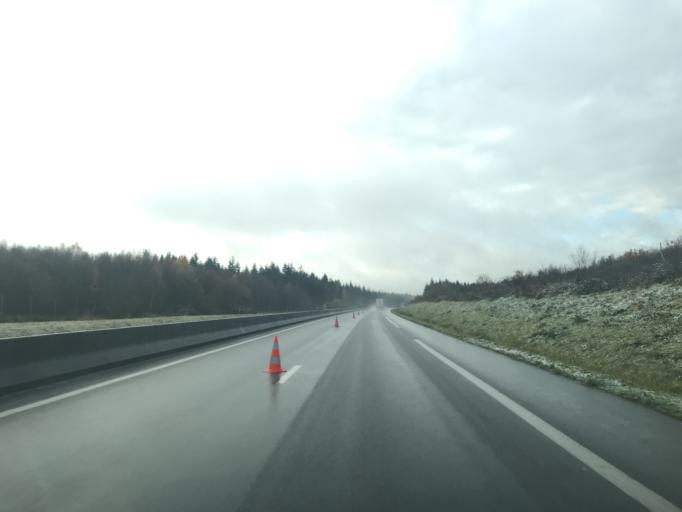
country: FR
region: Lower Normandy
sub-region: Departement de l'Orne
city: Gace
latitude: 48.8041
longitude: 0.3433
